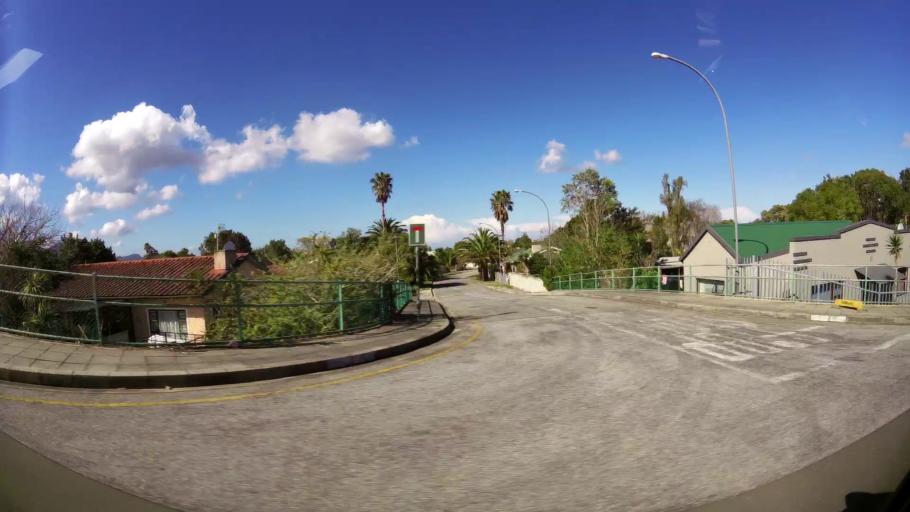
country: ZA
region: Western Cape
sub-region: Eden District Municipality
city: George
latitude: -33.9513
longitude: 22.4650
